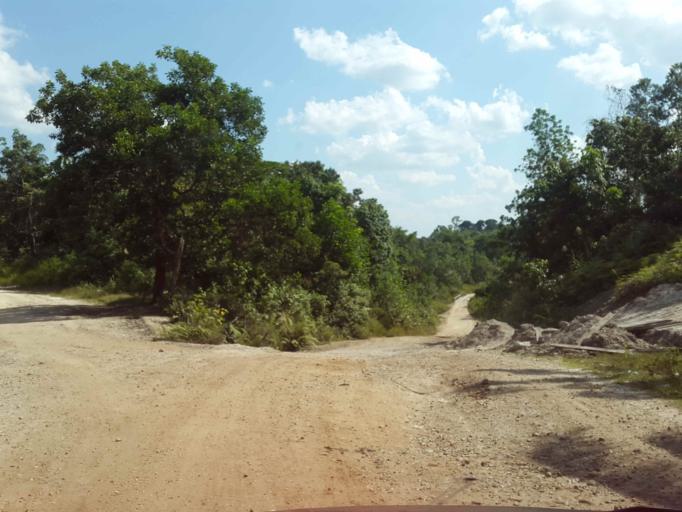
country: MY
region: Sarawak
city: Simanggang
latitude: 0.7205
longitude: 111.5591
